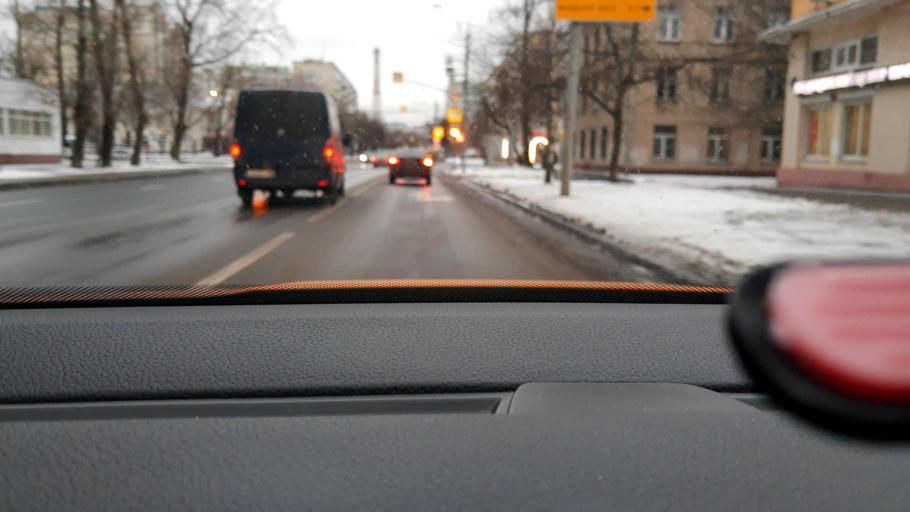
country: RU
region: Moscow
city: Strogino
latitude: 55.8431
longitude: 37.4381
